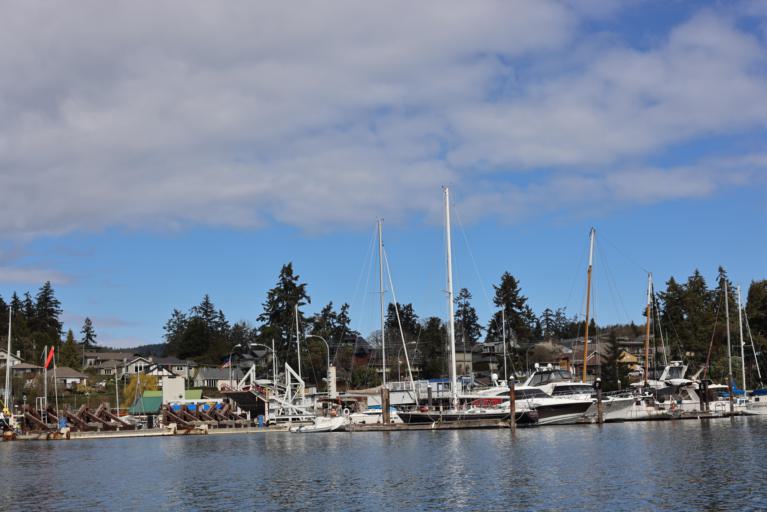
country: CA
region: British Columbia
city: North Saanich
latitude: 48.5763
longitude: -123.4679
